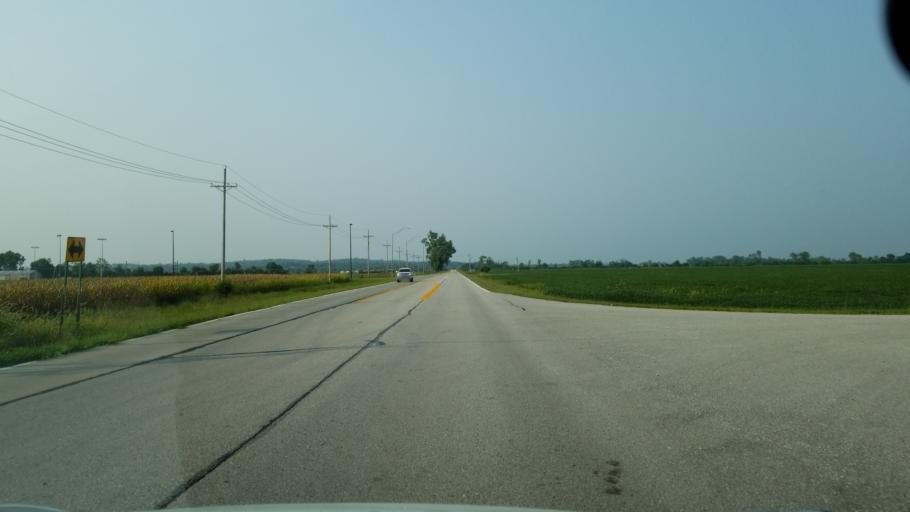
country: US
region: Nebraska
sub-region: Sarpy County
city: Bellevue
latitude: 41.1003
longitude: -95.8899
